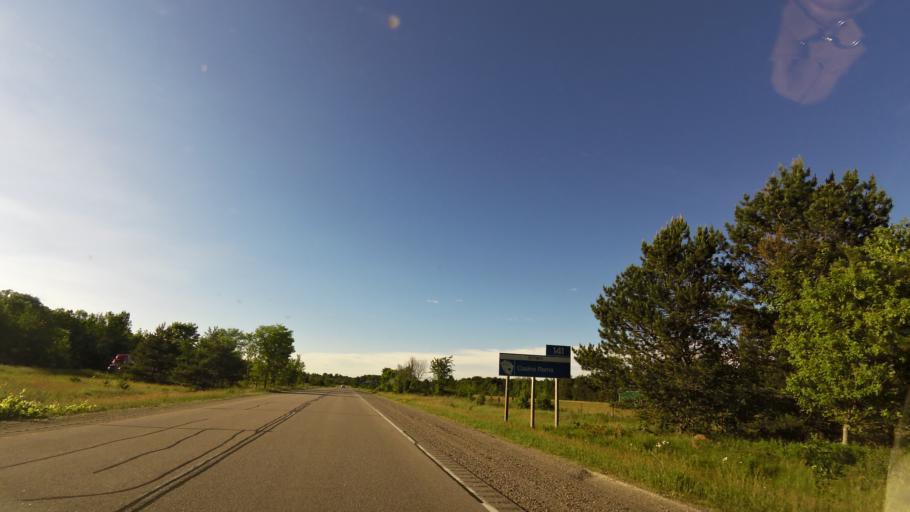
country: CA
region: Ontario
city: Orillia
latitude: 44.6872
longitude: -79.6473
